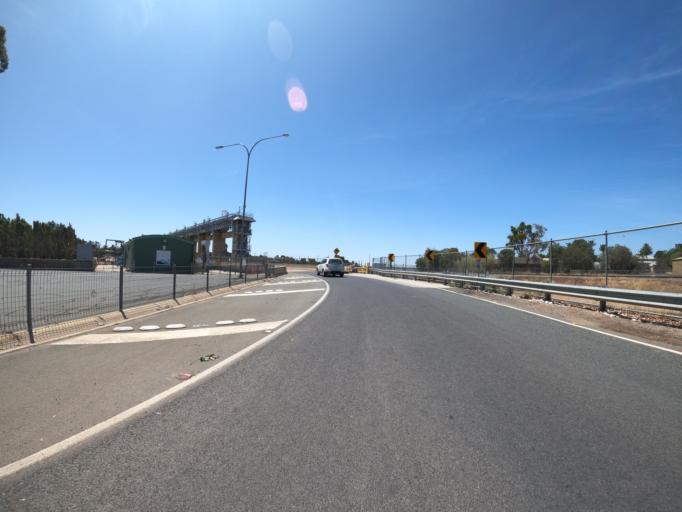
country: AU
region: Victoria
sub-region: Moira
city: Yarrawonga
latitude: -36.0099
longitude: 145.9995
